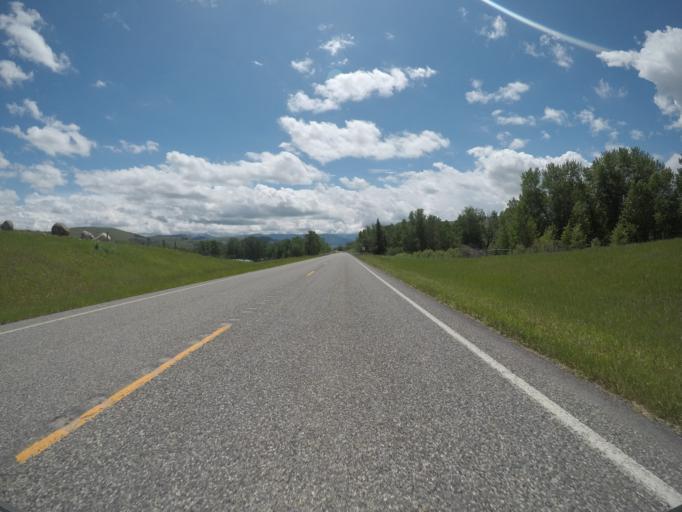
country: US
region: Montana
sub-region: Sweet Grass County
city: Big Timber
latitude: 45.6624
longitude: -110.1132
